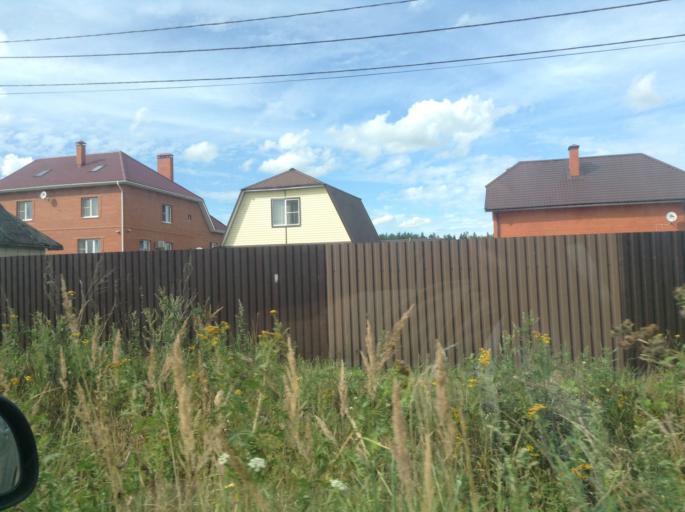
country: RU
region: Moskovskaya
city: Yegor'yevsk
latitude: 55.3655
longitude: 39.0958
